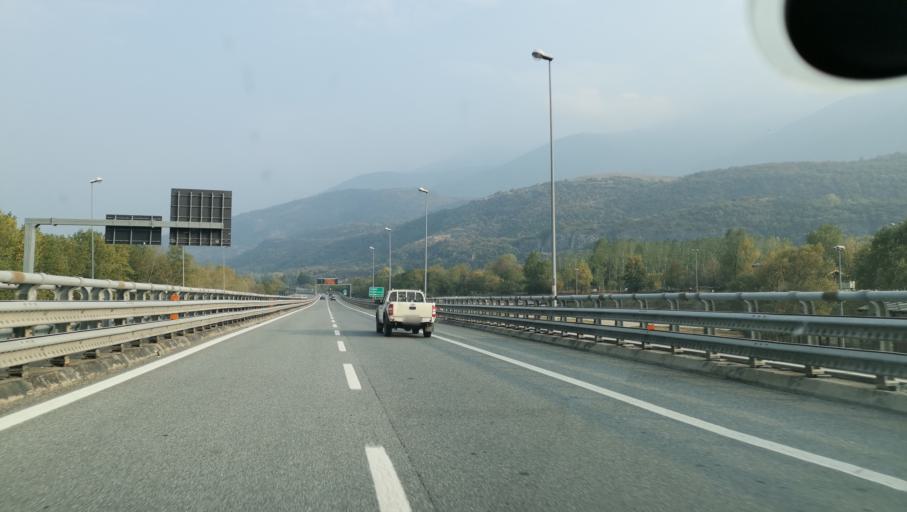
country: IT
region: Piedmont
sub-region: Provincia di Torino
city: Mattie
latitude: 45.1358
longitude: 7.0927
